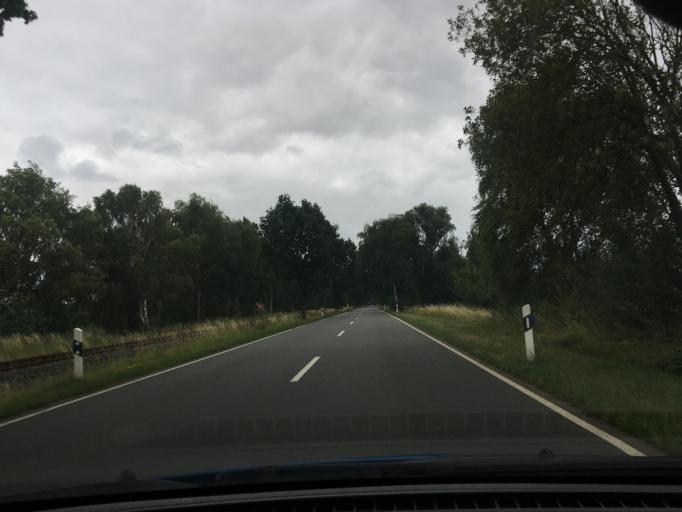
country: DE
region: Lower Saxony
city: Toppenstedt
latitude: 53.2709
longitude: 10.1211
